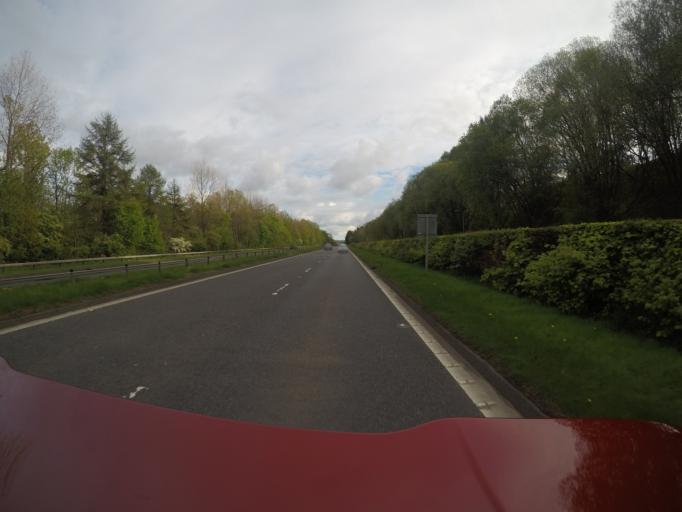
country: GB
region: Scotland
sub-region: West Dunbartonshire
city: Renton
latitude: 55.9730
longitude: -4.5877
